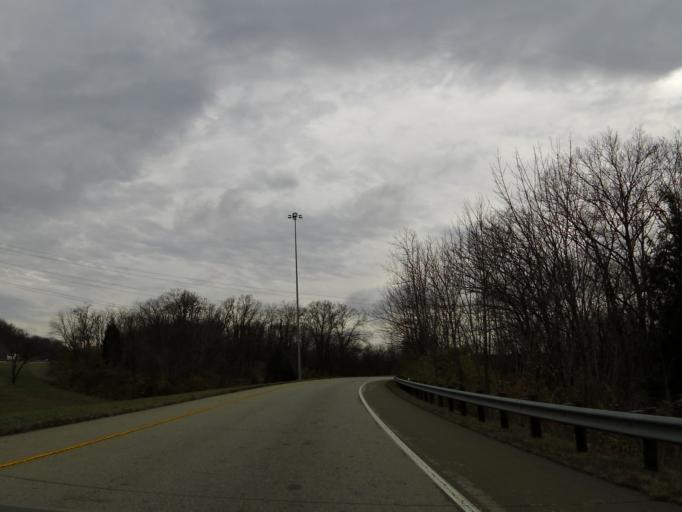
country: US
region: Ohio
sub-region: Hamilton County
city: Grandview
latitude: 39.2224
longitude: -84.7435
